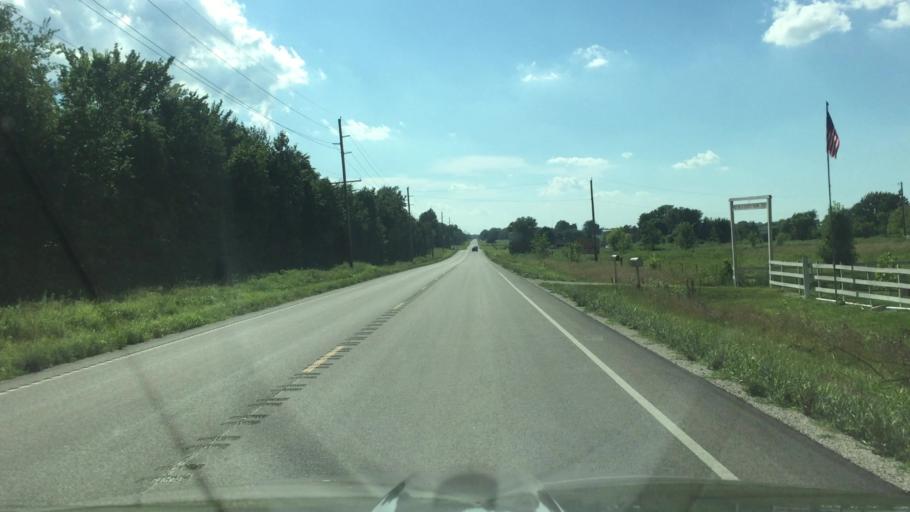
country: US
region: Missouri
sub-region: Morgan County
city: Versailles
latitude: 38.3944
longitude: -92.7168
